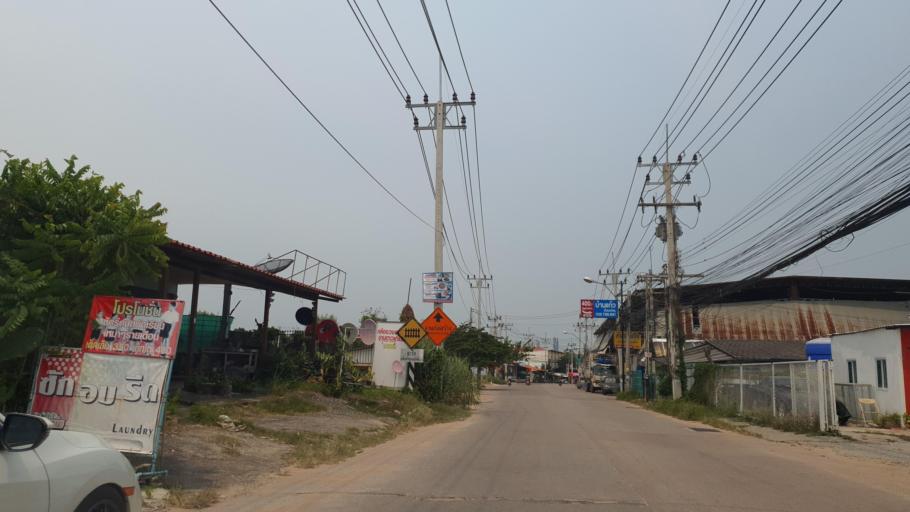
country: TH
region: Chon Buri
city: Phatthaya
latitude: 12.8999
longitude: 100.9030
